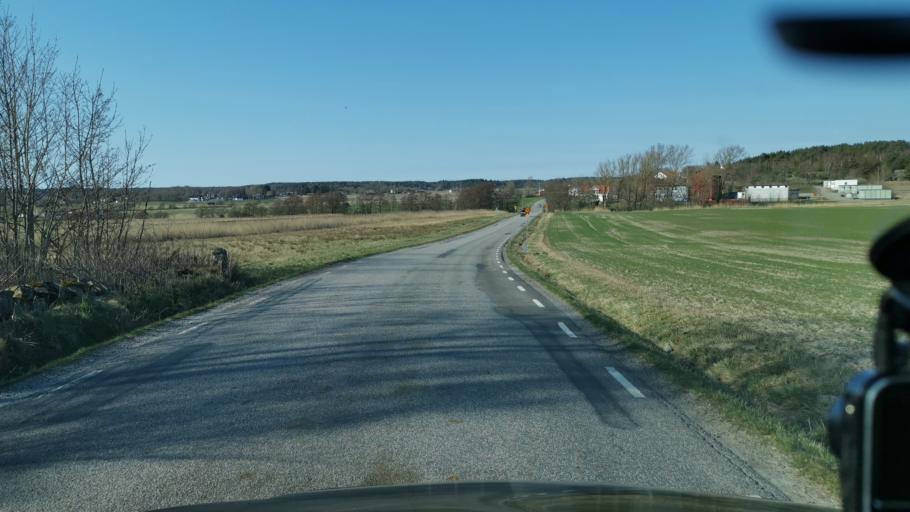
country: SE
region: Vaestra Goetaland
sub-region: Kungalvs Kommun
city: Kode
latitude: 57.9411
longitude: 11.8207
